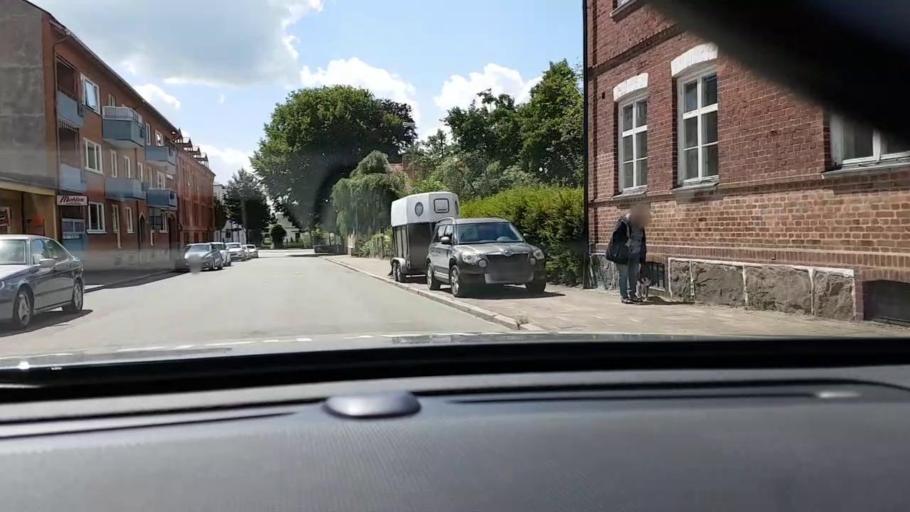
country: SE
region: Skane
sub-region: Hassleholms Kommun
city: Hassleholm
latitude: 56.1550
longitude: 13.7678
